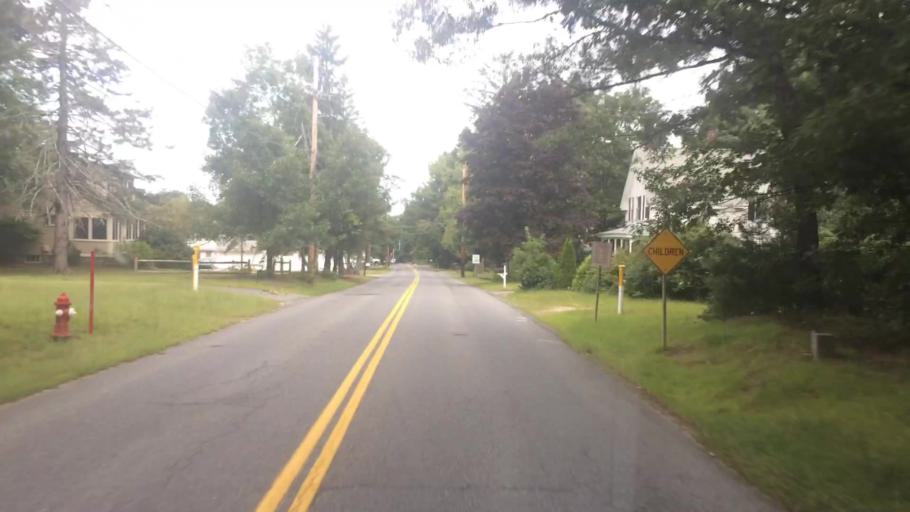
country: US
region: Massachusetts
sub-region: Middlesex County
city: West Concord
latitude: 42.4596
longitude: -71.4139
